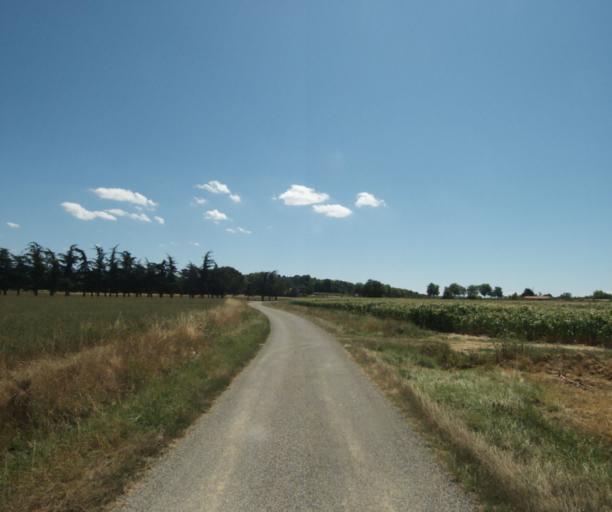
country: FR
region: Midi-Pyrenees
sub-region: Departement de la Haute-Garonne
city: Revel
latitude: 43.4493
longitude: 1.9495
